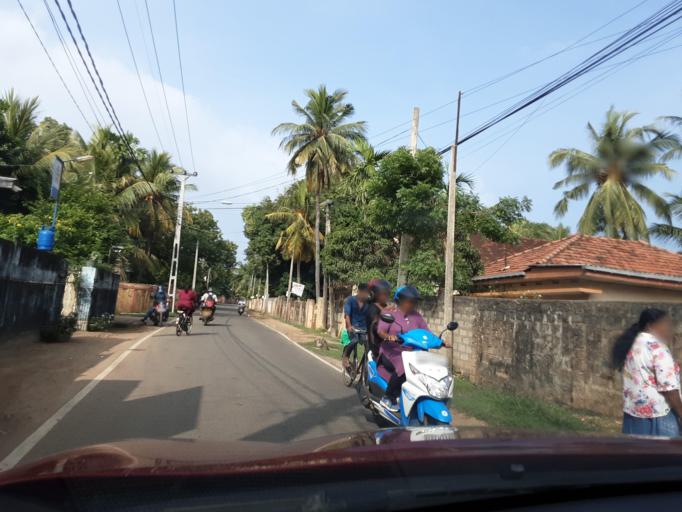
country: LK
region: Northern Province
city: Jaffna
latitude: 9.6698
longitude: 80.0242
